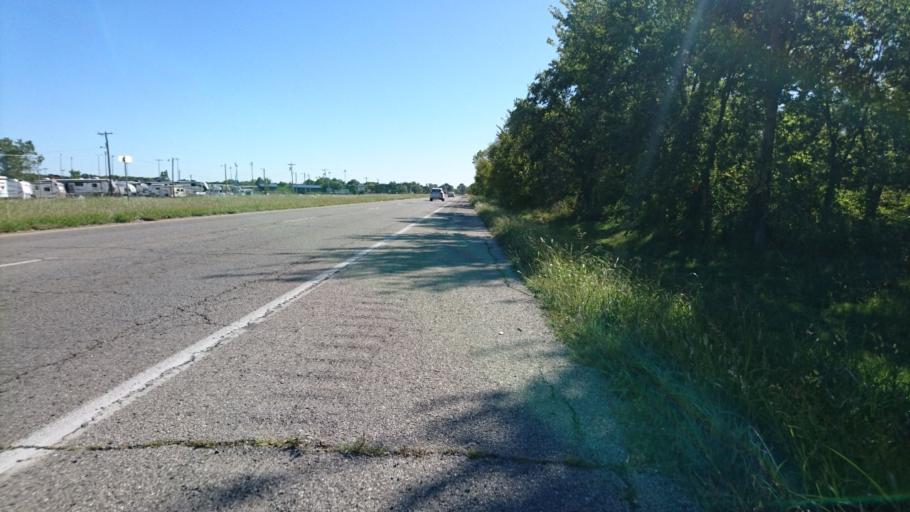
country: US
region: Oklahoma
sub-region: Rogers County
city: Justice
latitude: 36.3788
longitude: -95.5594
